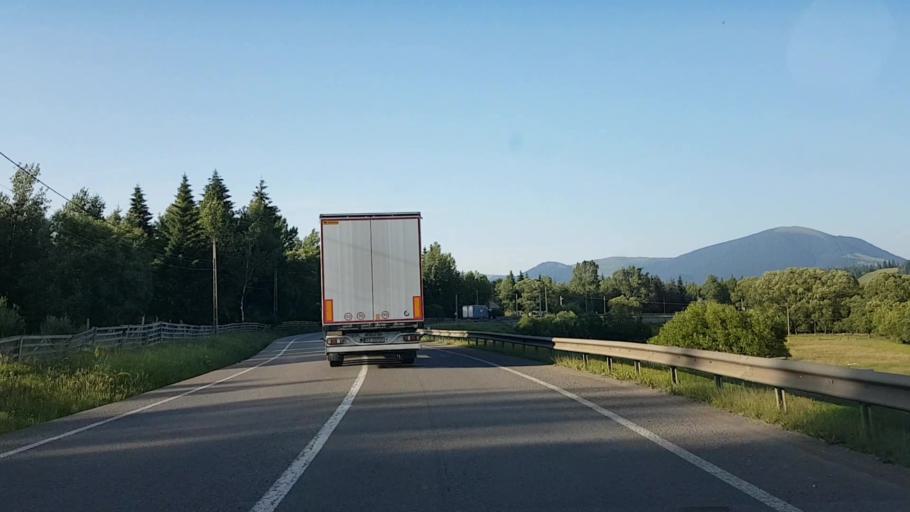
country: RO
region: Suceava
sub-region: Comuna Poiana Stampei
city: Poiana Stampei
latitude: 47.3355
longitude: 25.1637
